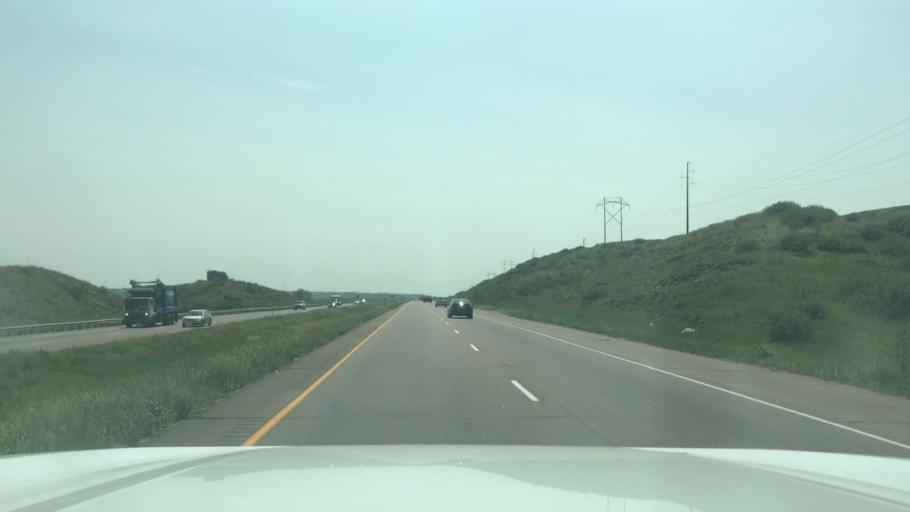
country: US
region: Colorado
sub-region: El Paso County
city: Security-Widefield
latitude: 38.7359
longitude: -104.7443
